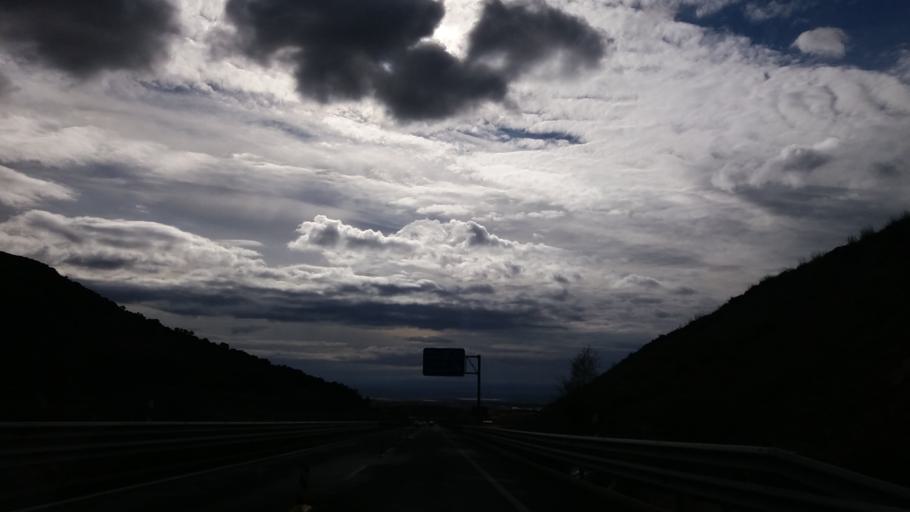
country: ES
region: Aragon
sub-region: Provincia de Huesca
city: Nueno
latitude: 42.2760
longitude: -0.4331
